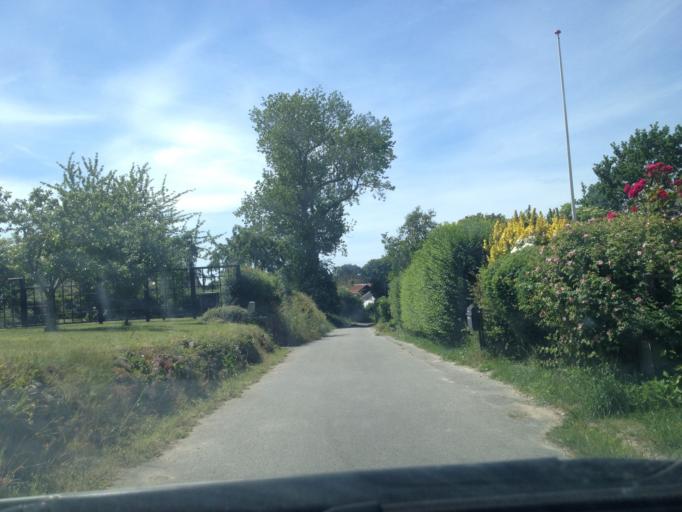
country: DK
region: Central Jutland
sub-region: Samso Kommune
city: Tranebjerg
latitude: 55.8633
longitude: 10.6432
